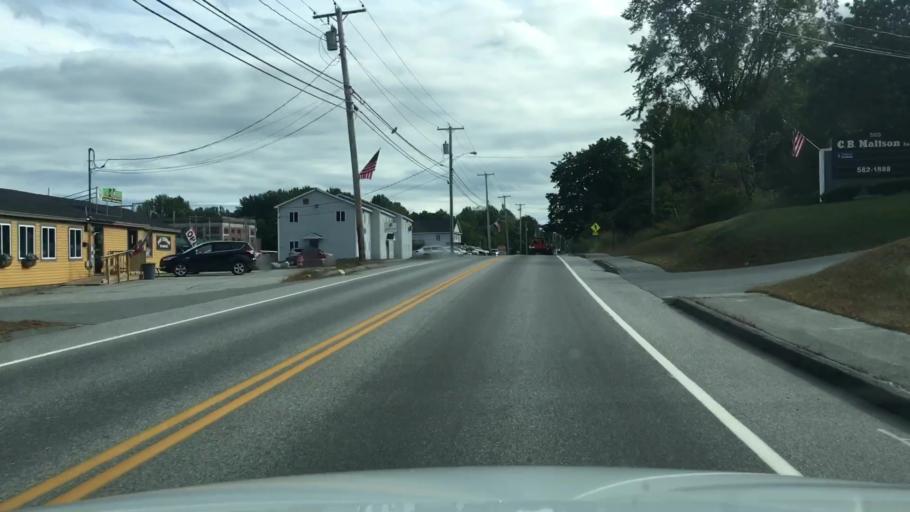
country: US
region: Maine
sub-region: Kennebec County
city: Farmingdale
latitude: 44.2461
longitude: -69.7709
